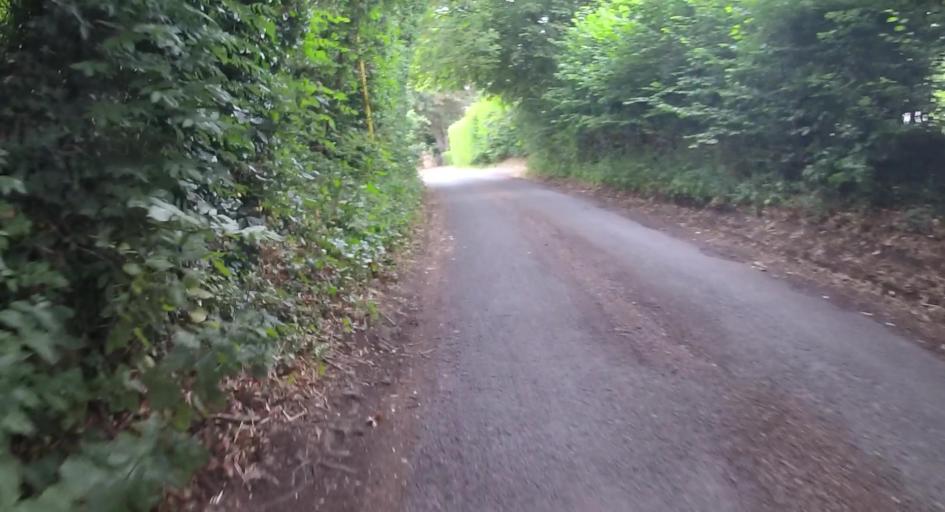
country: GB
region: England
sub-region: Hampshire
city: Swanmore
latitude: 51.0282
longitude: -1.1591
